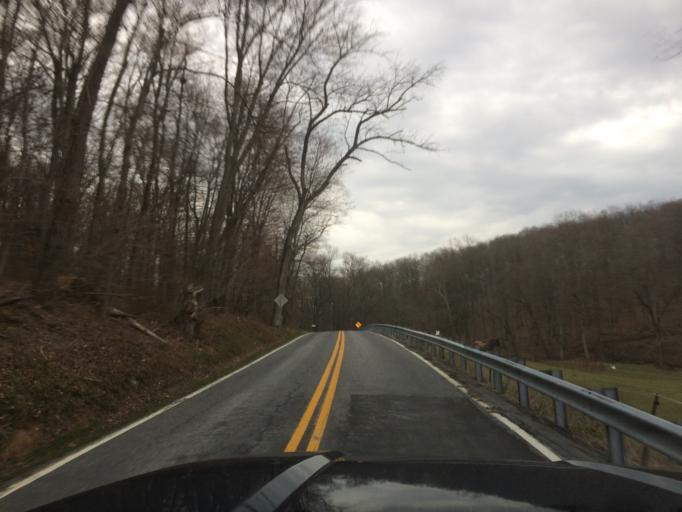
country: US
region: Maryland
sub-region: Frederick County
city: Woodsboro
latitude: 39.4998
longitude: -77.2847
